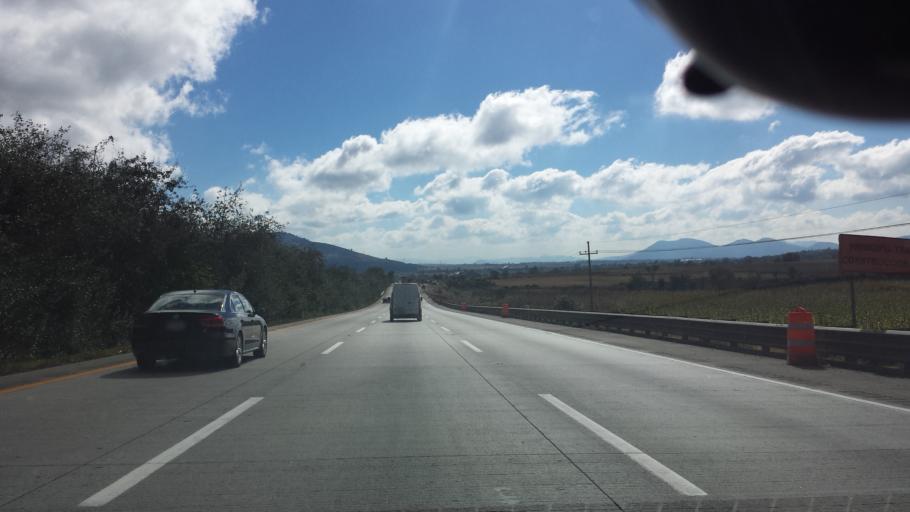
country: MX
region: Mexico
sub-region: Jilotepec
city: La Comunidad
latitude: 20.0330
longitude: -99.5534
